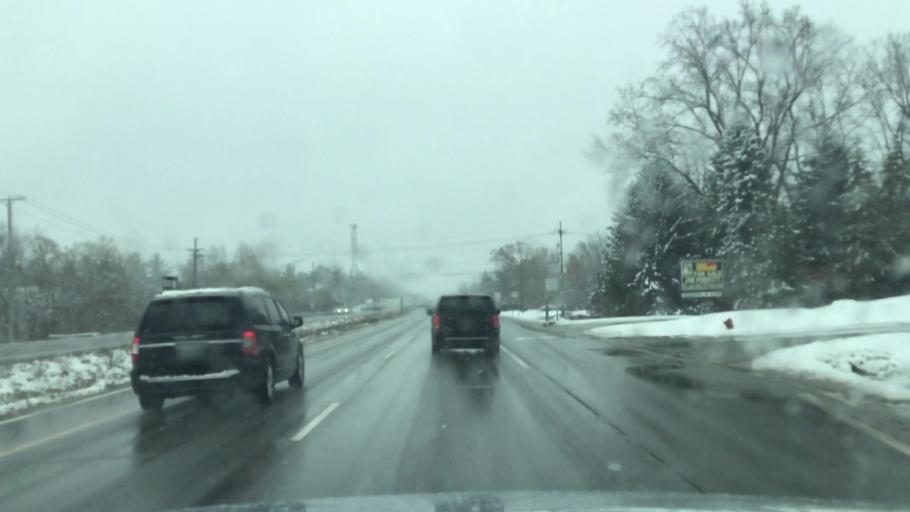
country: US
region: Michigan
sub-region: Oakland County
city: Lake Orion
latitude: 42.7373
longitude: -83.2452
